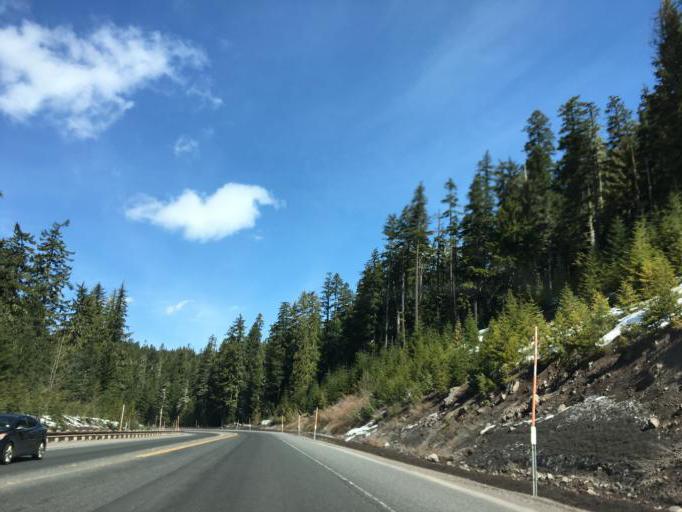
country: US
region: Oregon
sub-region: Clackamas County
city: Mount Hood Village
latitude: 45.2980
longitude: -121.7335
